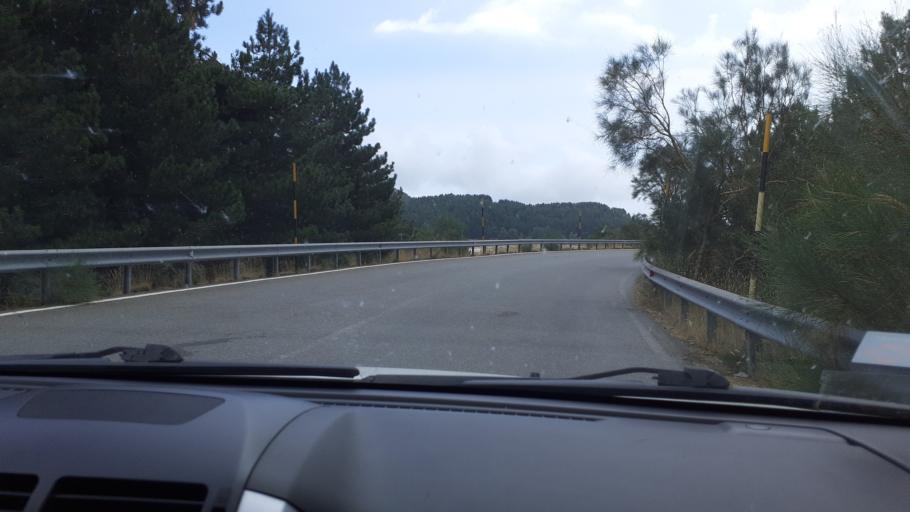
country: IT
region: Sicily
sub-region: Catania
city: Nicolosi
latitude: 37.6976
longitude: 15.0177
